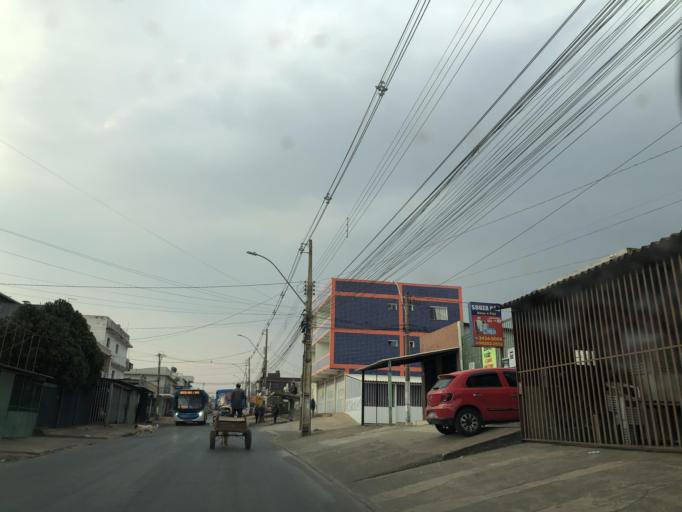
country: BR
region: Federal District
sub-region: Brasilia
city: Brasilia
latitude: -15.9199
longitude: -48.0612
